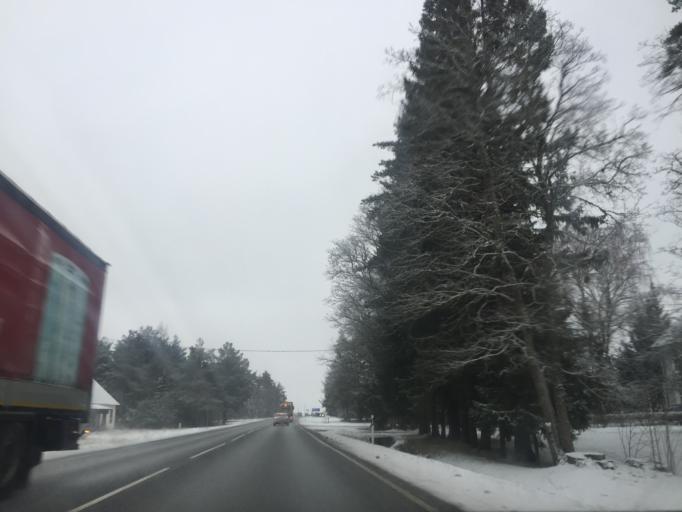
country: EE
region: Laeaene
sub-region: Lihula vald
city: Lihula
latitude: 58.6613
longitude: 23.7288
